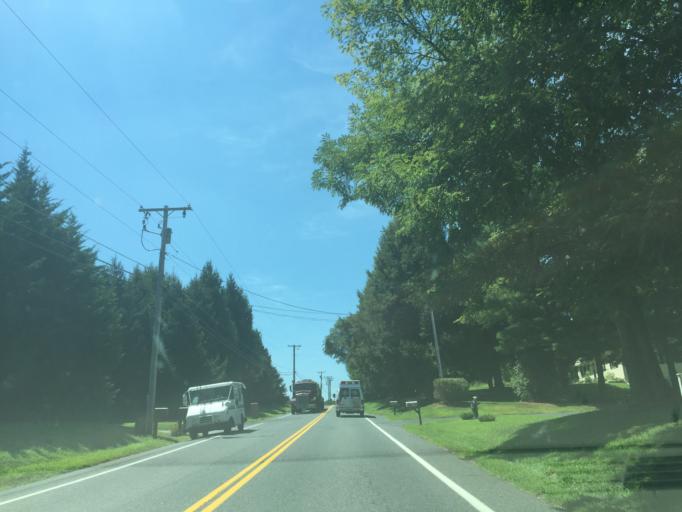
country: US
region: Maryland
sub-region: Harford County
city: Bel Air North
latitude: 39.6008
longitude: -76.3891
